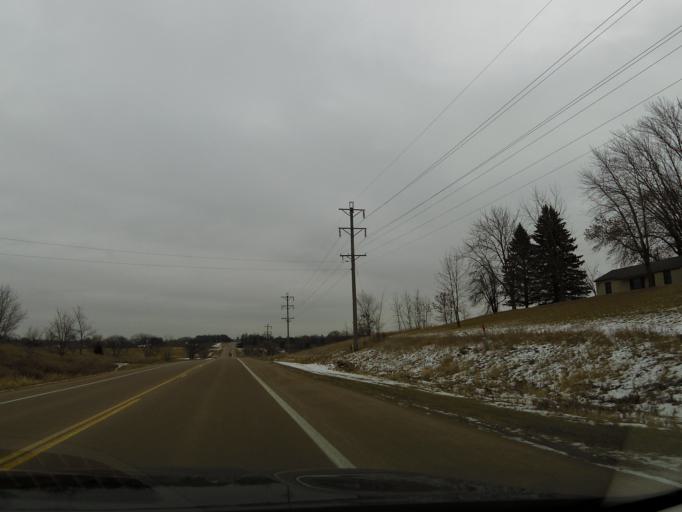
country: US
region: Minnesota
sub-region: Carver County
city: Watertown
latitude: 44.9631
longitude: -93.8161
